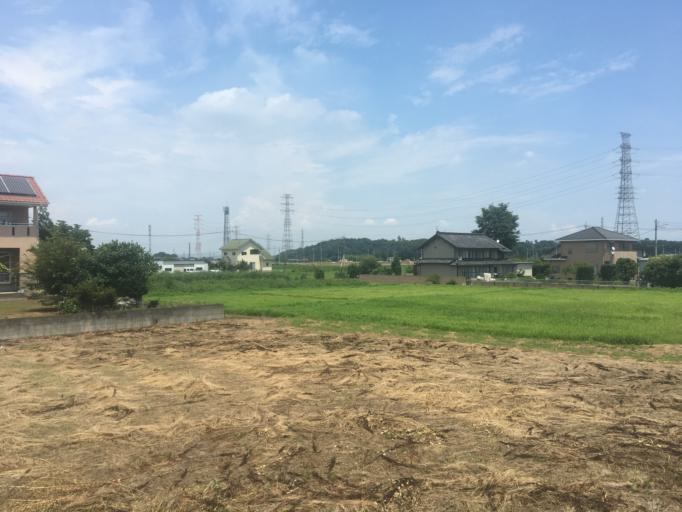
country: JP
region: Saitama
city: Kodamacho-kodamaminami
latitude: 36.1723
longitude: 139.1832
